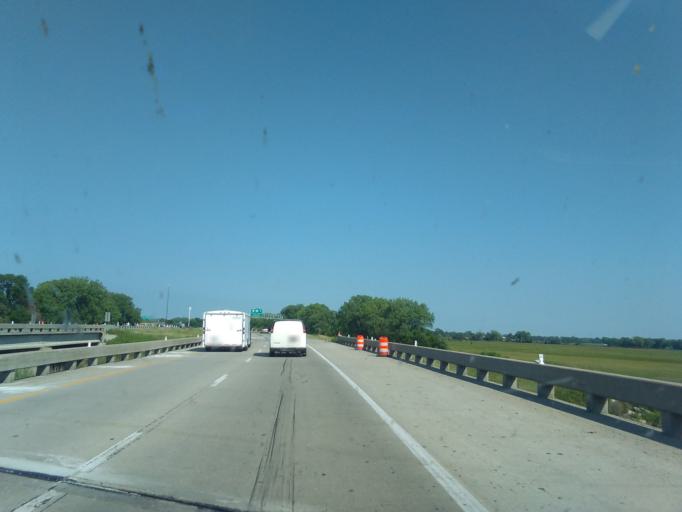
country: US
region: Nebraska
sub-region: Hall County
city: Grand Island
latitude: 40.8202
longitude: -98.3912
